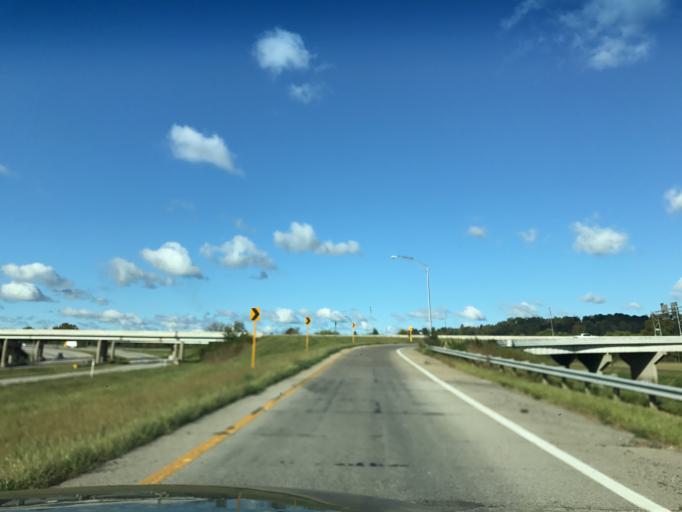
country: US
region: Ohio
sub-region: Athens County
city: Athens
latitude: 39.3318
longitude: -82.0806
